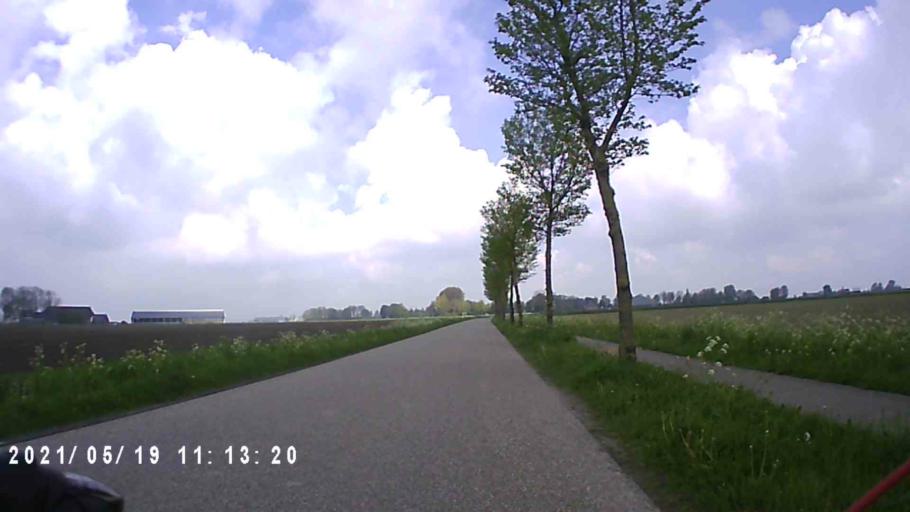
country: NL
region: Groningen
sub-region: Gemeente Zuidhorn
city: Grijpskerk
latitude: 53.2920
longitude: 6.2436
